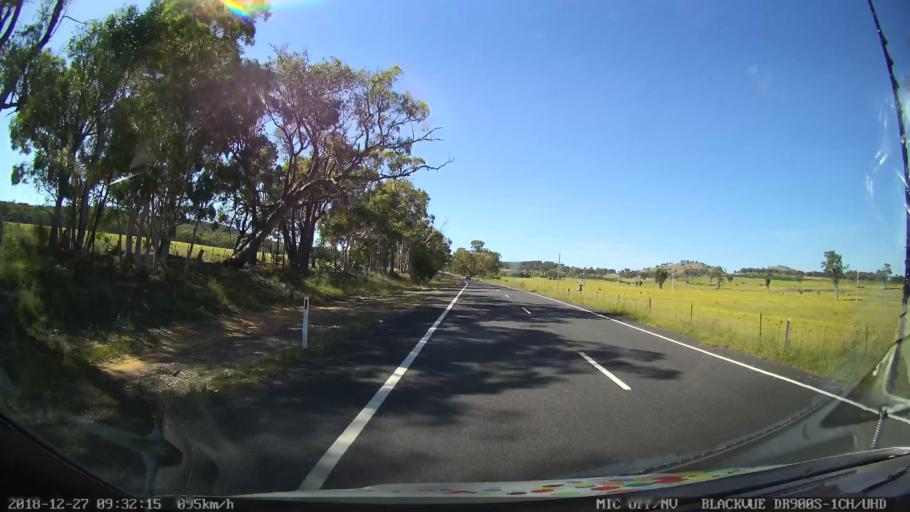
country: AU
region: New South Wales
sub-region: Lithgow
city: Portland
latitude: -33.2044
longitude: 150.0152
